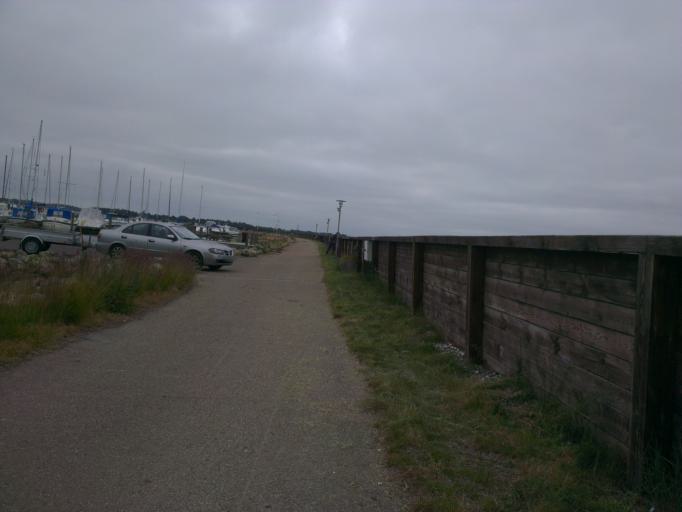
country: DK
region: Capital Region
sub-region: Frederikssund Kommune
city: Frederikssund
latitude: 55.8278
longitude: 12.0576
